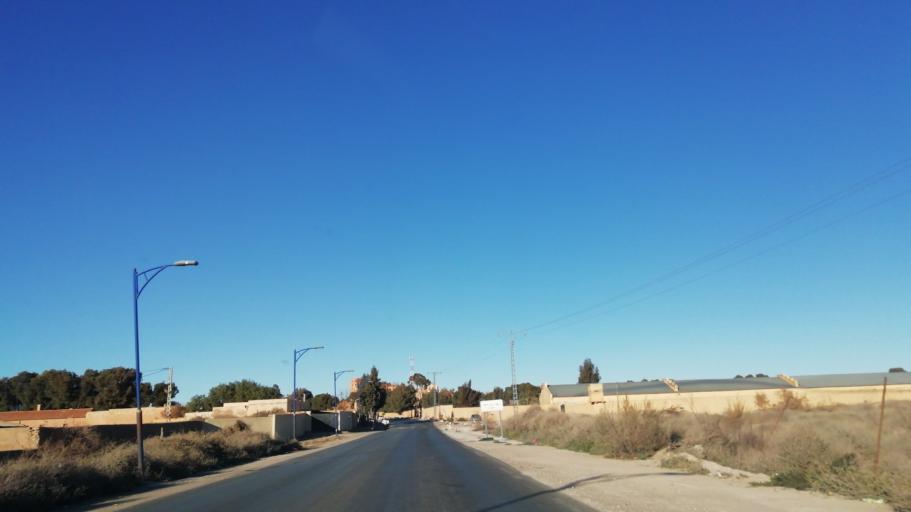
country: DZ
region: Saida
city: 'Ain el Hadjar
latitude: 34.1421
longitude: 0.0711
